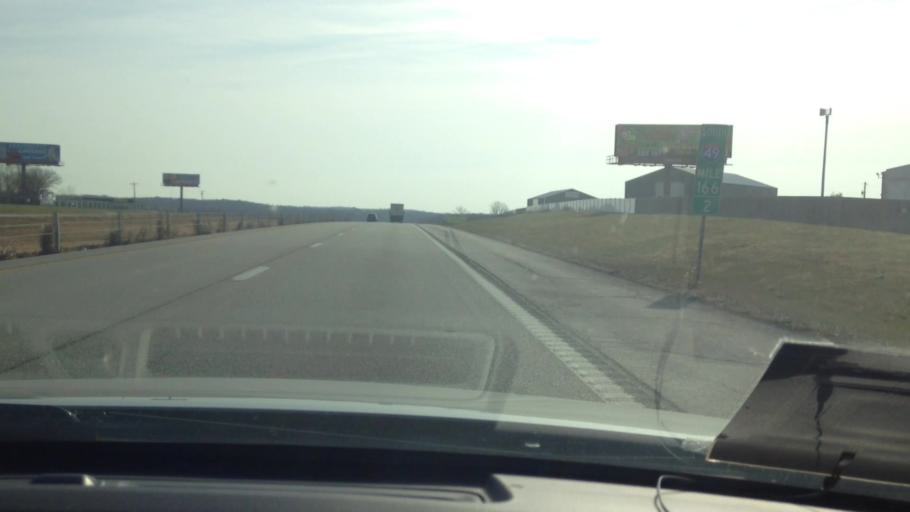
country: US
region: Missouri
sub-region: Cass County
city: Peculiar
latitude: 38.7106
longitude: -94.4435
